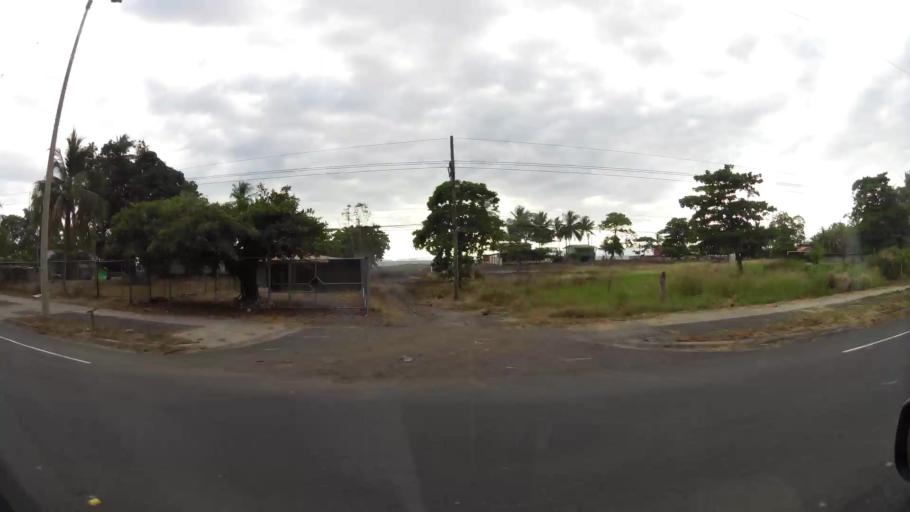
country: CR
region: Puntarenas
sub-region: Canton Central de Puntarenas
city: Chacarita
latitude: 9.9367
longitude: -84.7246
